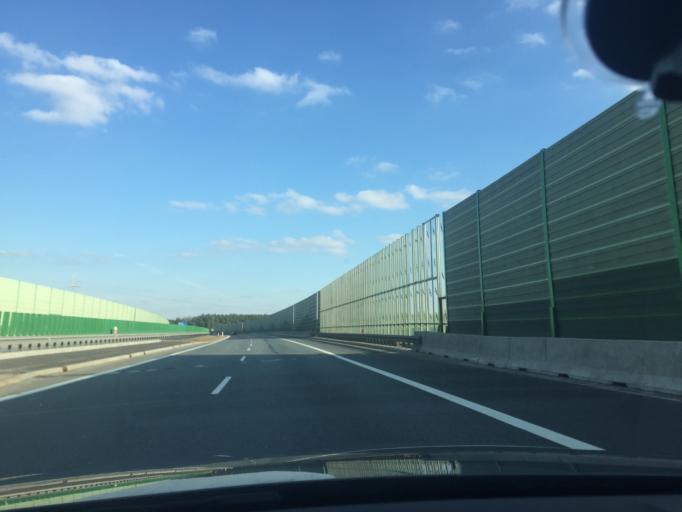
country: PL
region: Lubusz
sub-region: Powiat slubicki
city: Rzepin
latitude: 52.3285
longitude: 14.8405
